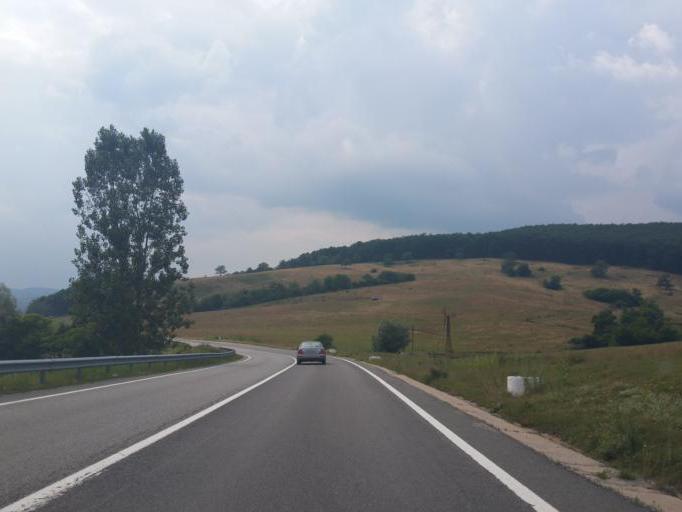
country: RO
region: Salaj
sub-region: Comuna Romanasi
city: Romanasi
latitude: 47.1235
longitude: 23.1533
